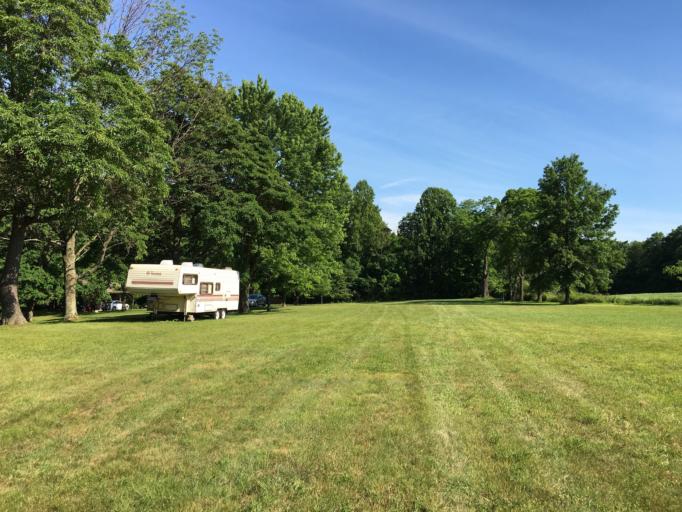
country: US
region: Ohio
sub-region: Geauga County
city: Middlefield
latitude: 41.4010
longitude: -81.0179
